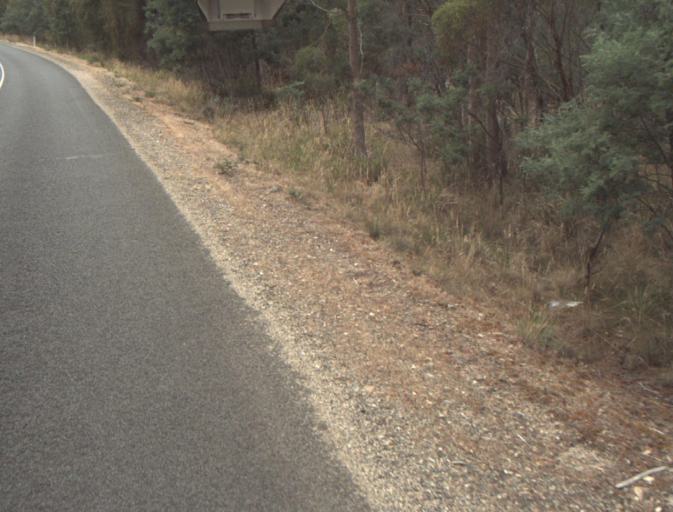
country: AU
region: Tasmania
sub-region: Northern Midlands
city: Evandale
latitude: -41.5094
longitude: 147.3491
